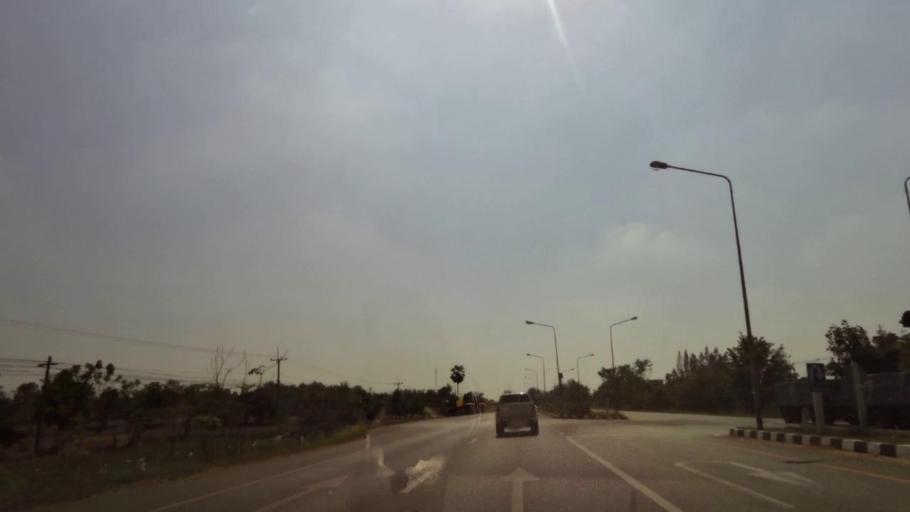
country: TH
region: Phichit
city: Wachira Barami
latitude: 16.4261
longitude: 100.1445
